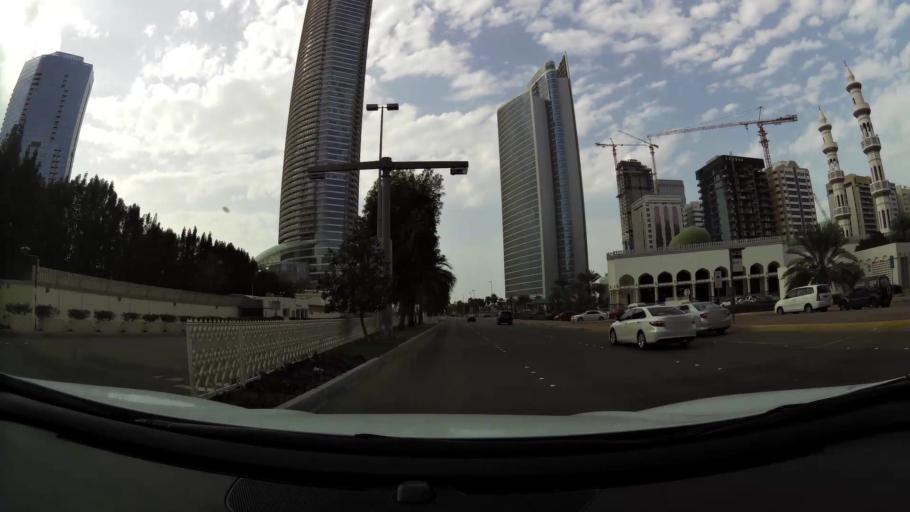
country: AE
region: Abu Dhabi
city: Abu Dhabi
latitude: 24.4838
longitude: 54.3529
